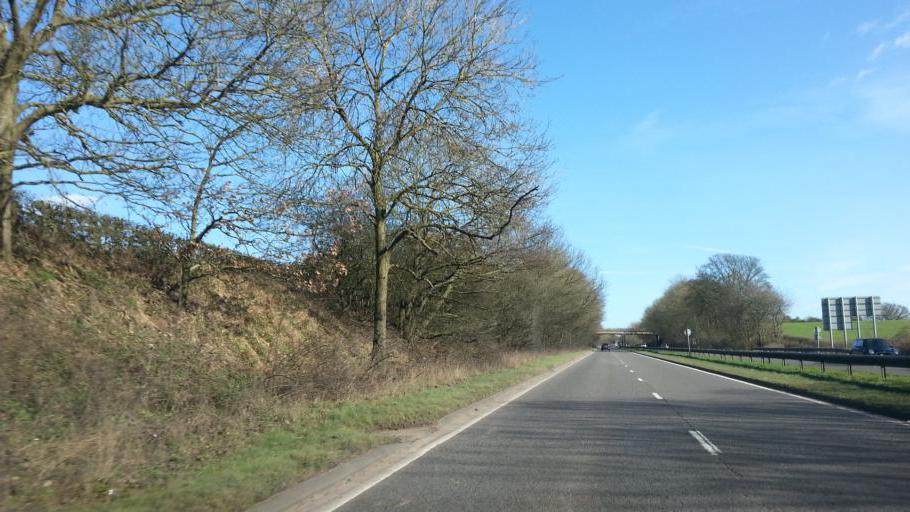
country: GB
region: England
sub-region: Solihull
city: Meriden
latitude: 52.4415
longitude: -1.6356
